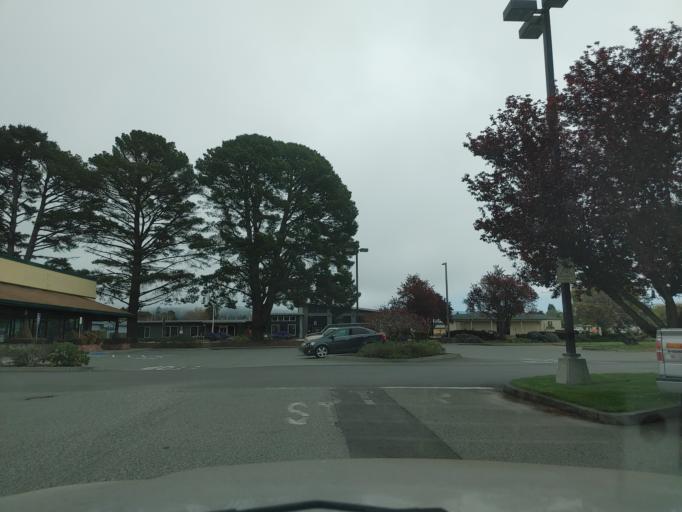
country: US
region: California
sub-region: Humboldt County
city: McKinleyville
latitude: 40.9437
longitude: -124.1018
